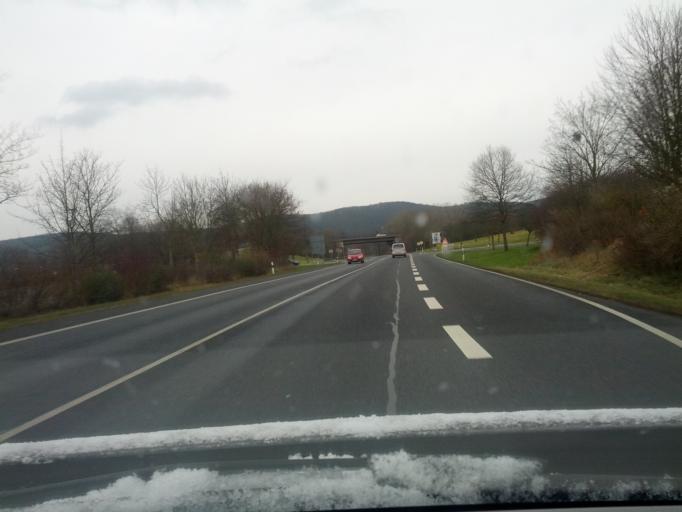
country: DE
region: Hesse
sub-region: Regierungsbezirk Kassel
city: Bad Sooden-Allendorf
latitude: 51.2691
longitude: 9.9696
